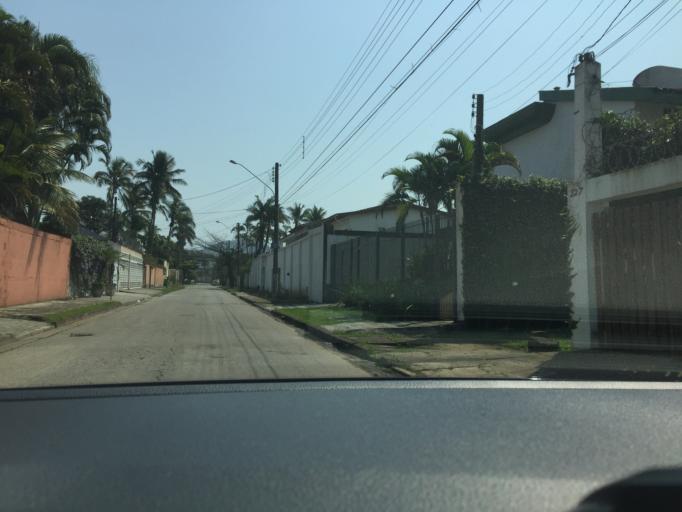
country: BR
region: Sao Paulo
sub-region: Guaruja
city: Guaruja
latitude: -23.9834
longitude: -46.2160
